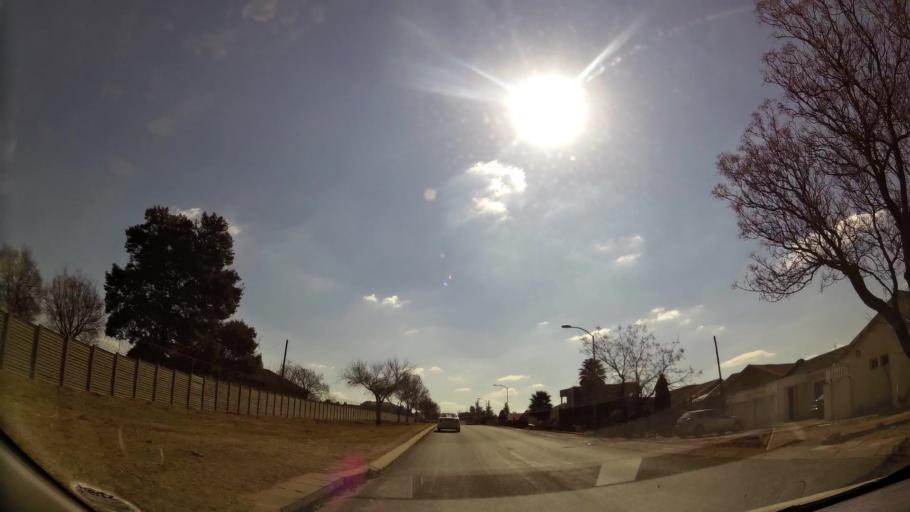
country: ZA
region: Gauteng
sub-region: West Rand District Municipality
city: Randfontein
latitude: -26.1774
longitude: 27.7481
